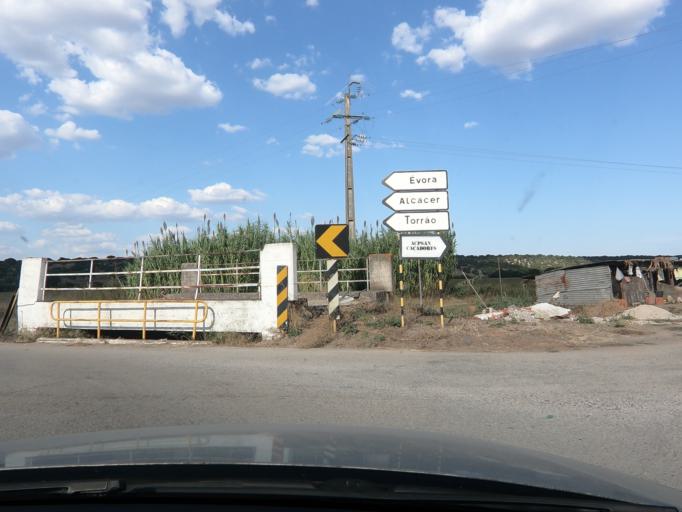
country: PT
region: Setubal
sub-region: Alcacer do Sal
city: Alcacer do Sal
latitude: 38.2479
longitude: -8.3578
